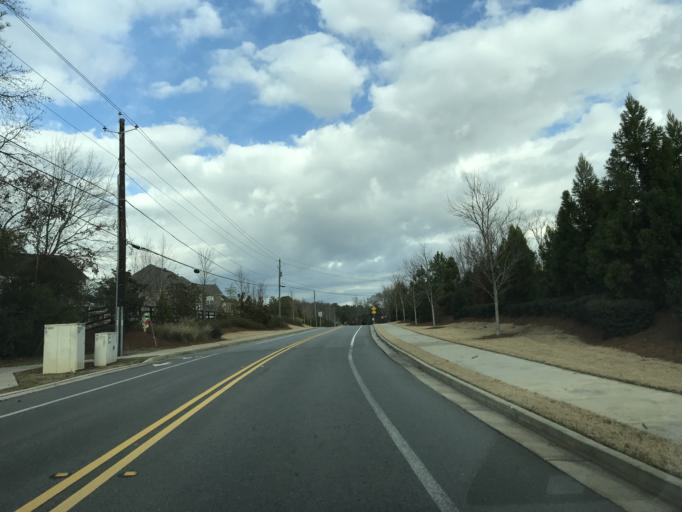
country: US
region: Georgia
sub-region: Fulton County
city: Alpharetta
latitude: 34.0904
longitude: -84.3122
